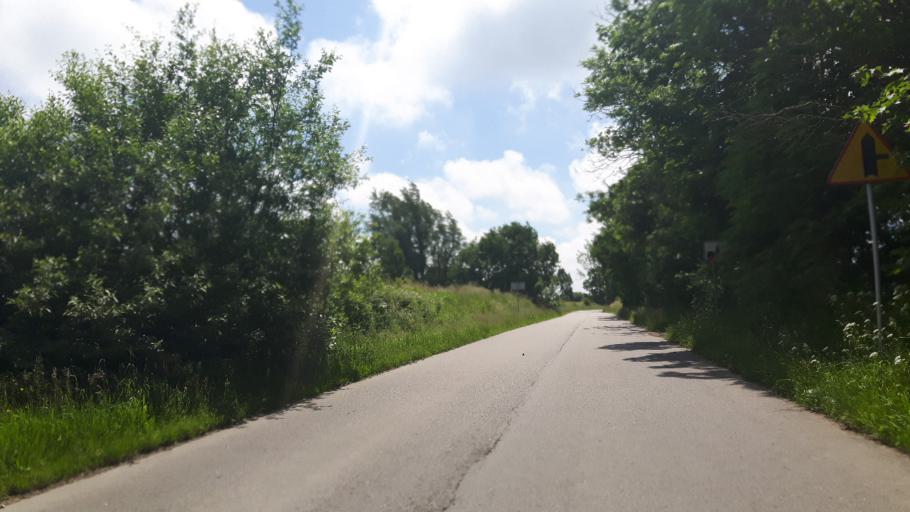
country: PL
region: West Pomeranian Voivodeship
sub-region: Powiat slawienski
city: Slawno
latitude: 54.5082
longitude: 16.6230
